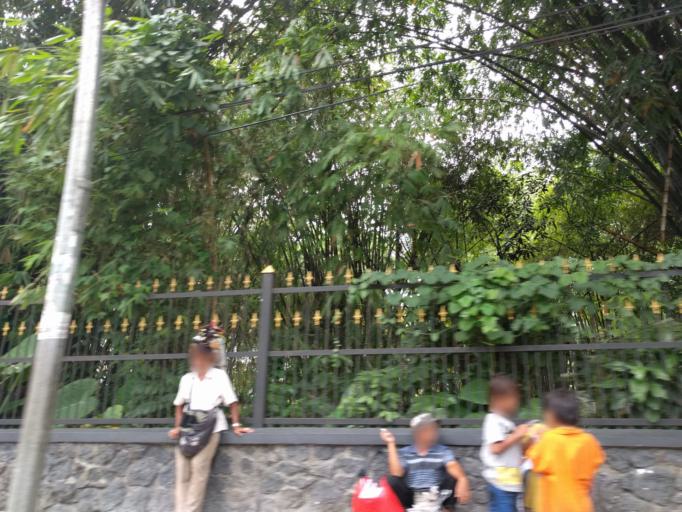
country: ID
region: West Java
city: Bogor
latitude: -6.5994
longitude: 106.7946
